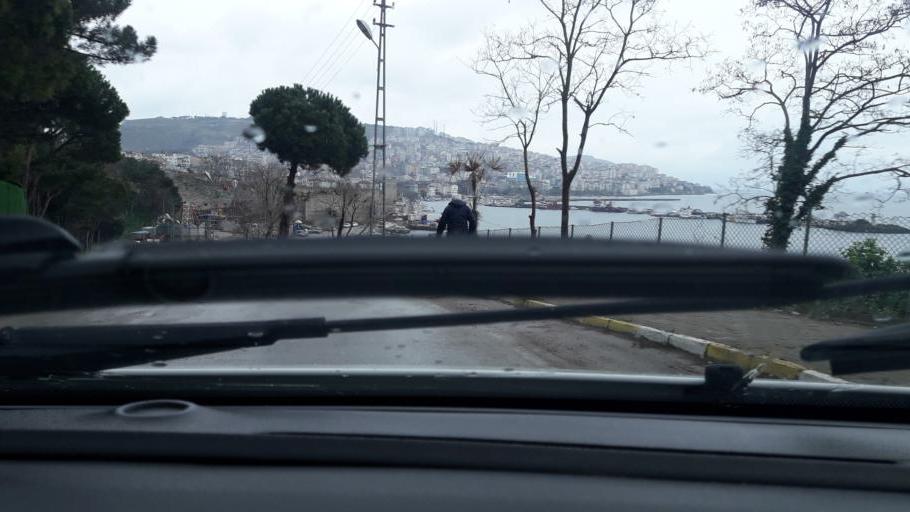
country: TR
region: Sinop
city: Sinop
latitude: 42.0232
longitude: 35.1393
